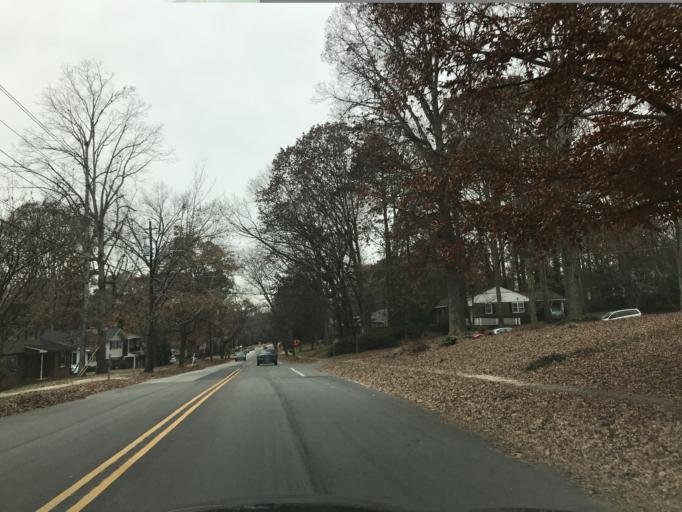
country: US
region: North Carolina
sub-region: Wake County
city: West Raleigh
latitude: 35.8372
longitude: -78.6198
